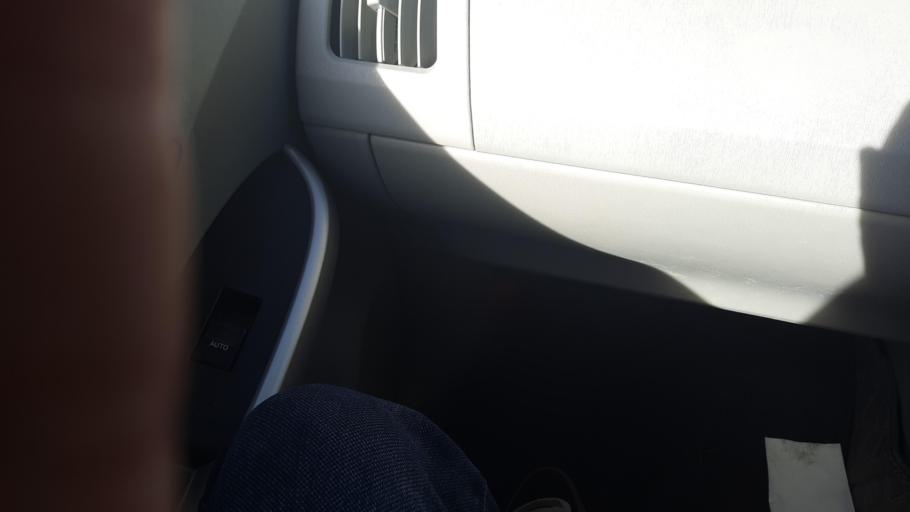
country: MN
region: Orhon
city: Erdenet
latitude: 49.0351
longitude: 104.0516
